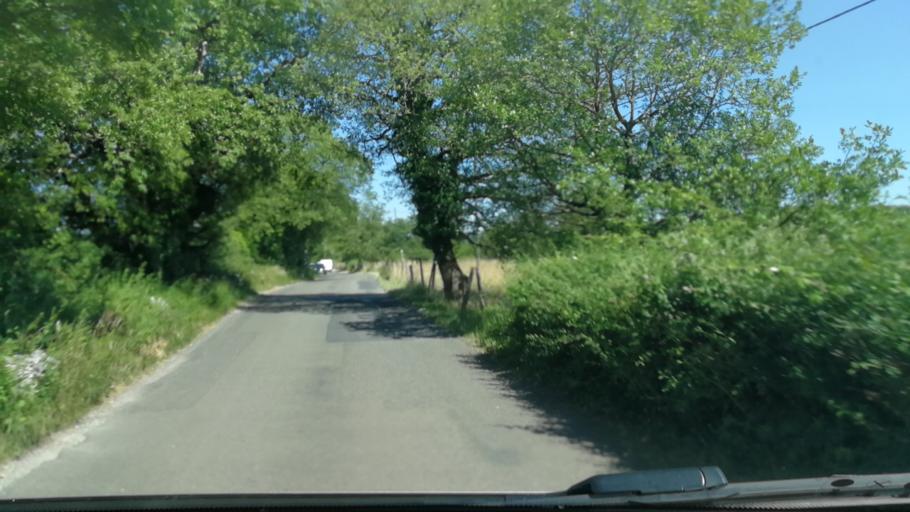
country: FR
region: Midi-Pyrenees
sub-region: Departement de l'Aveyron
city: Salles-la-Source
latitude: 44.4227
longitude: 2.5500
